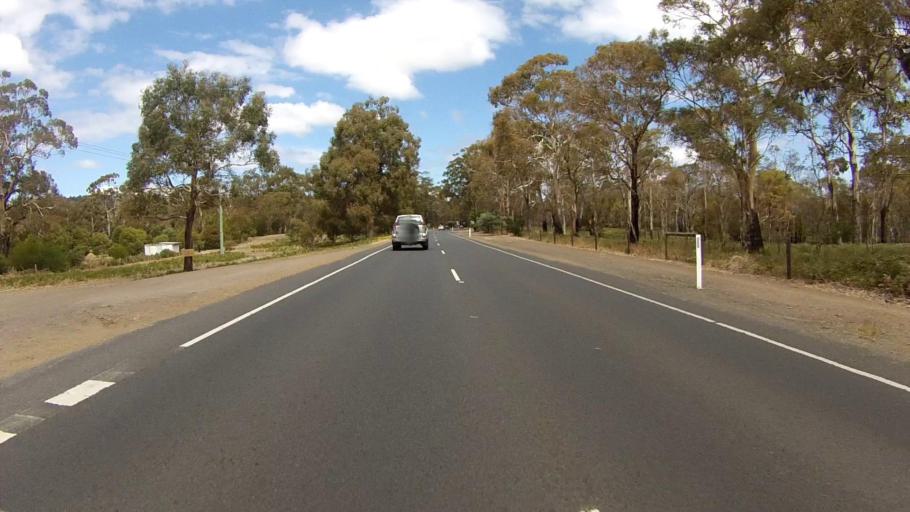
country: AU
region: Tasmania
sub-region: Sorell
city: Sorell
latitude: -42.8447
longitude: 147.6261
